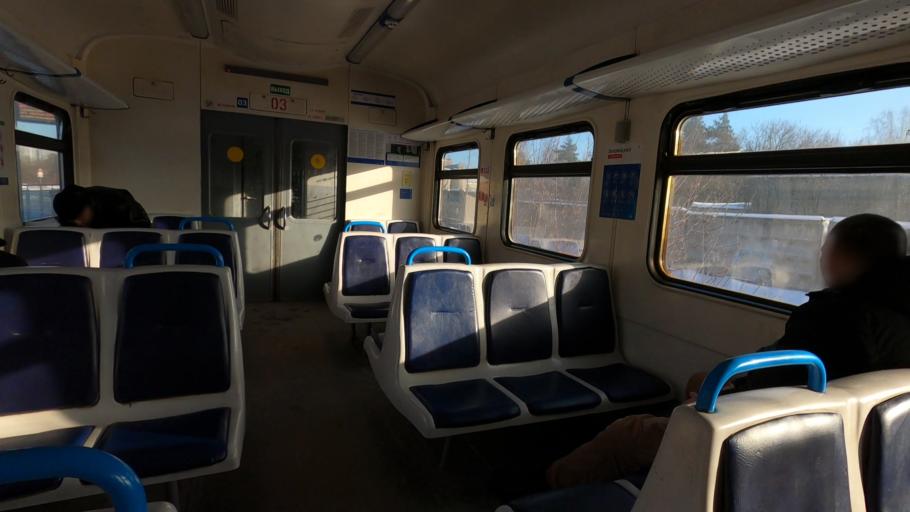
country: RU
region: Moskovskaya
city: Pavlovskiy Posad
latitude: 55.7744
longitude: 38.6994
